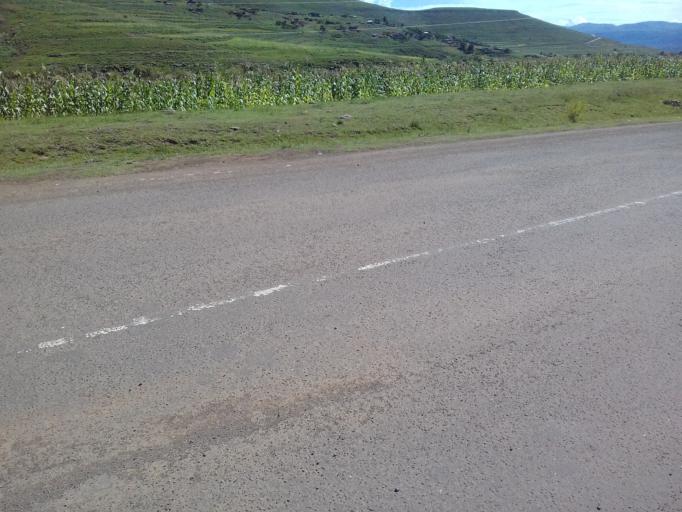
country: LS
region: Thaba-Tseka
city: Thaba-Tseka
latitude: -29.5209
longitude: 28.5825
